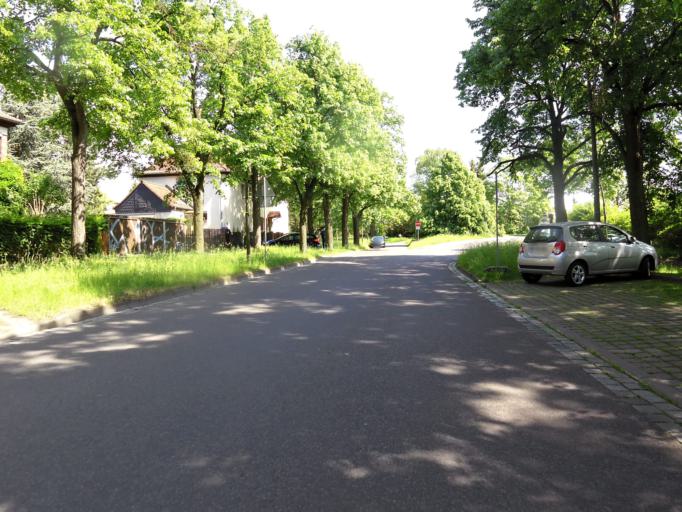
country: DE
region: Saxony
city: Leipzig
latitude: 51.3111
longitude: 12.4261
